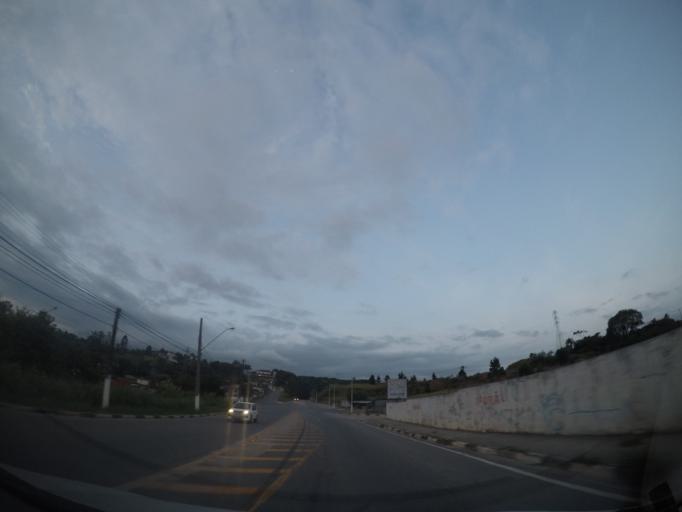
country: BR
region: Sao Paulo
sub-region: Aruja
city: Aruja
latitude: -23.3857
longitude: -46.3081
